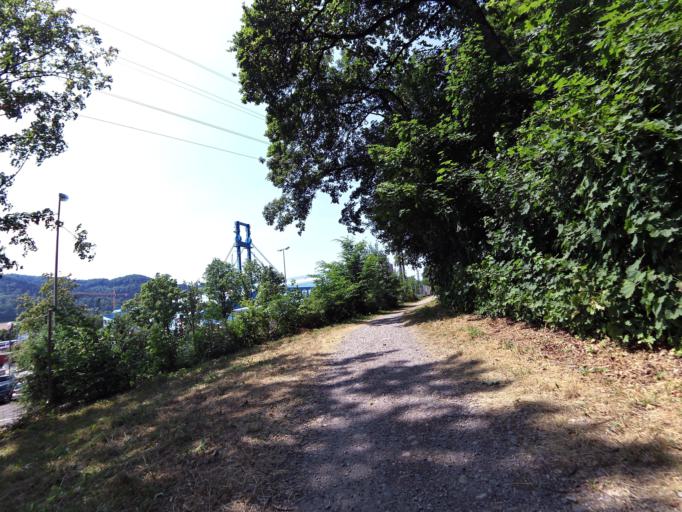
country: CH
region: Aargau
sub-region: Bezirk Baden
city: Killwangen
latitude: 47.4383
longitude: 8.3495
